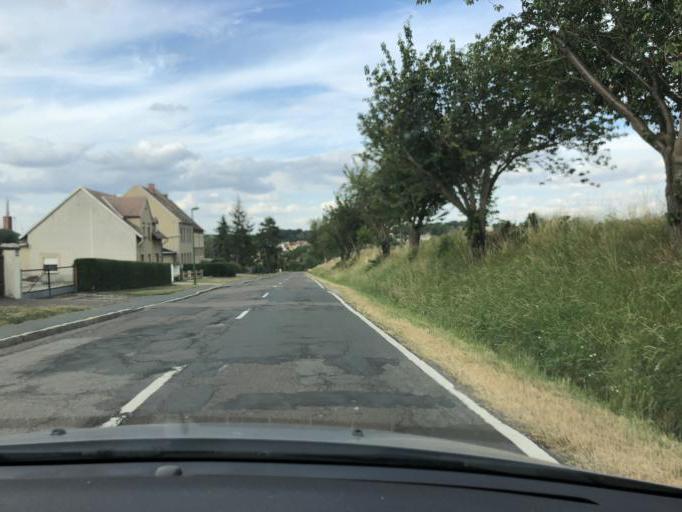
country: DE
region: Saxony-Anhalt
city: Osterfeld
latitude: 51.0737
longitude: 11.9194
